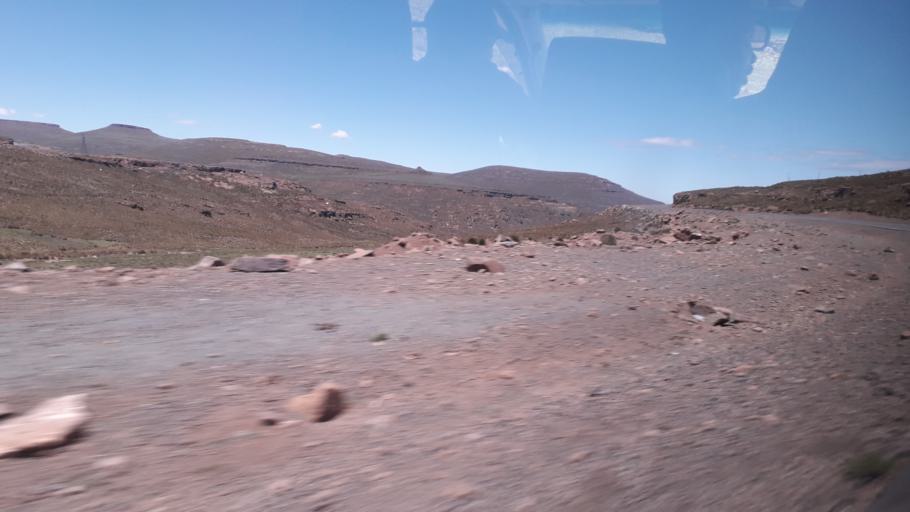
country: ZA
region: Orange Free State
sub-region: Thabo Mofutsanyana District Municipality
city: Phuthaditjhaba
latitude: -28.8259
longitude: 28.7405
